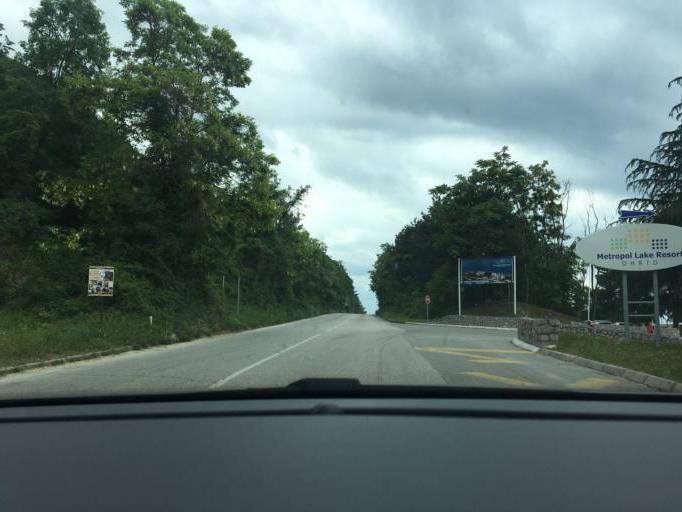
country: MK
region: Ohrid
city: Ohrid
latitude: 41.0583
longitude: 20.8030
